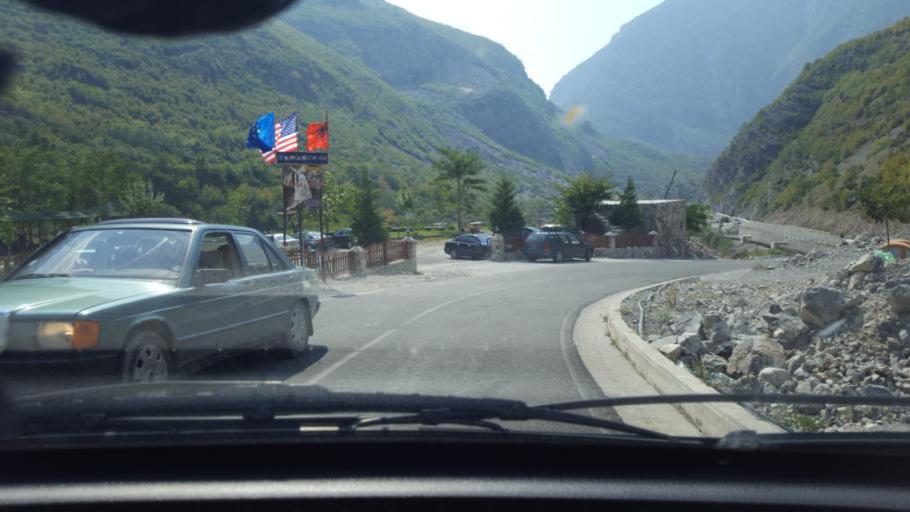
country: AL
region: Shkoder
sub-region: Rrethi i Malesia e Madhe
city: Kastrat
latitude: 42.5050
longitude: 19.5977
